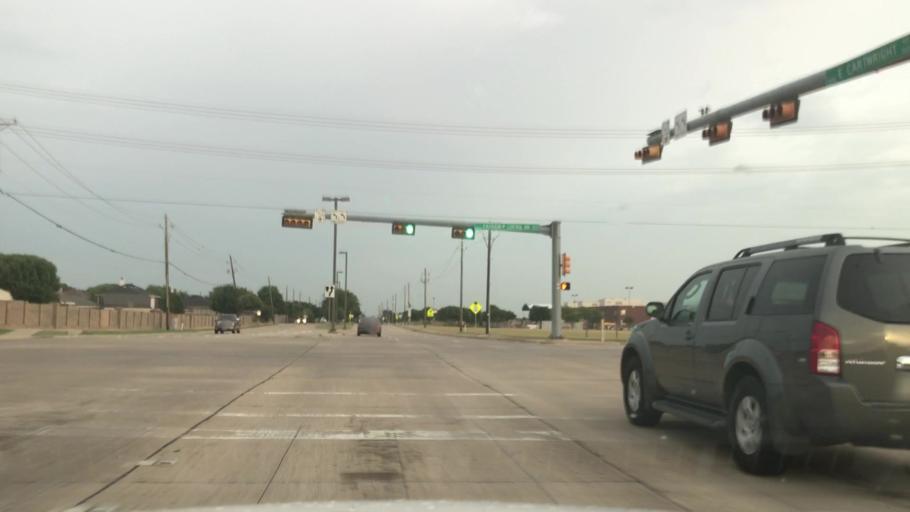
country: US
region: Texas
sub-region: Dallas County
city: Mesquite
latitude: 32.7350
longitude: -96.5593
